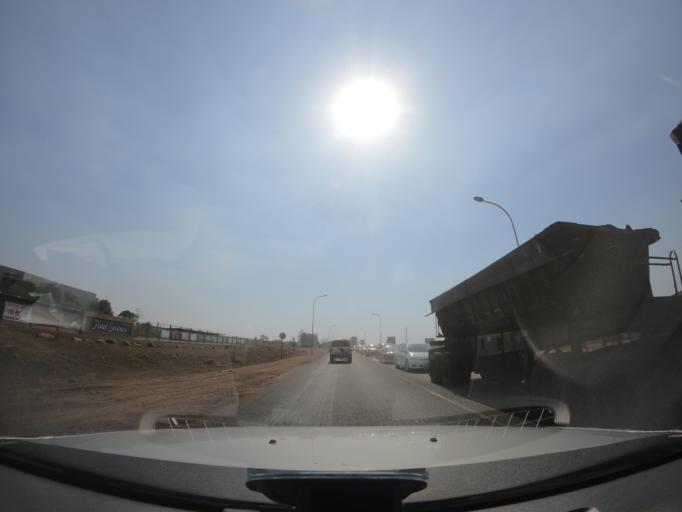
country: ZA
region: Mpumalanga
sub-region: Nkangala District Municipality
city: Middelburg
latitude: -25.8060
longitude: 29.4622
